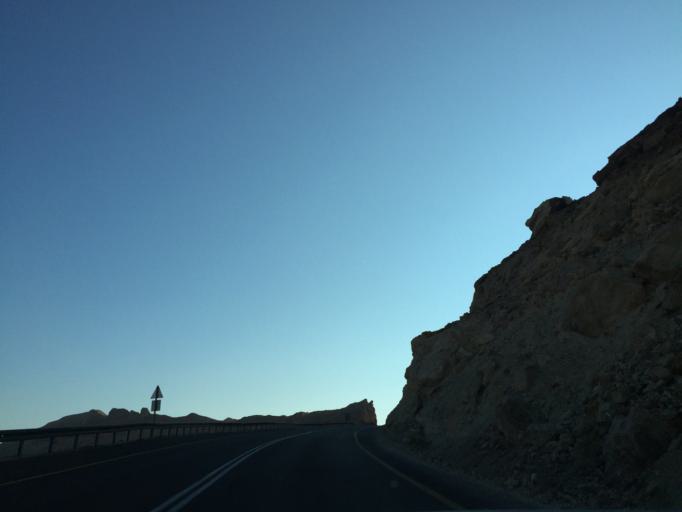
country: IL
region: Southern District
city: Mitzpe Ramon
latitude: 30.3207
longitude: 34.9620
